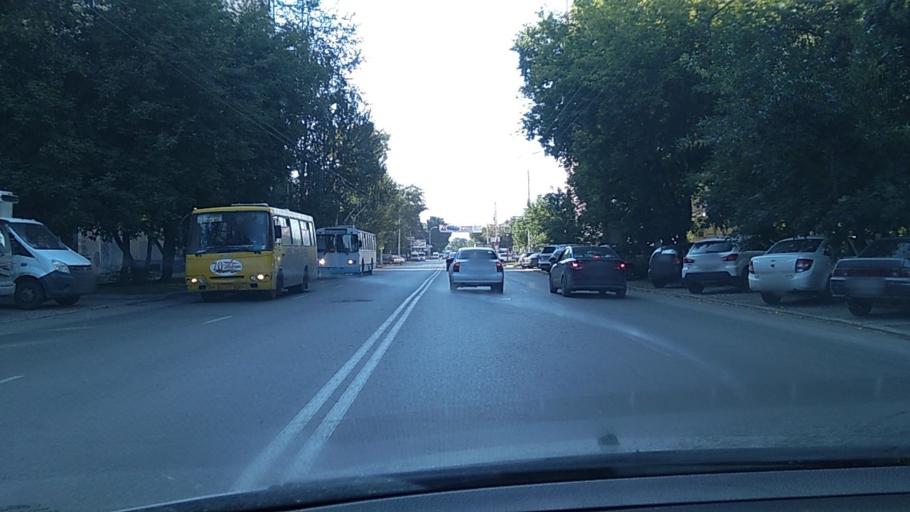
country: RU
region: Sverdlovsk
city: Yekaterinburg
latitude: 56.8619
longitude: 60.6375
